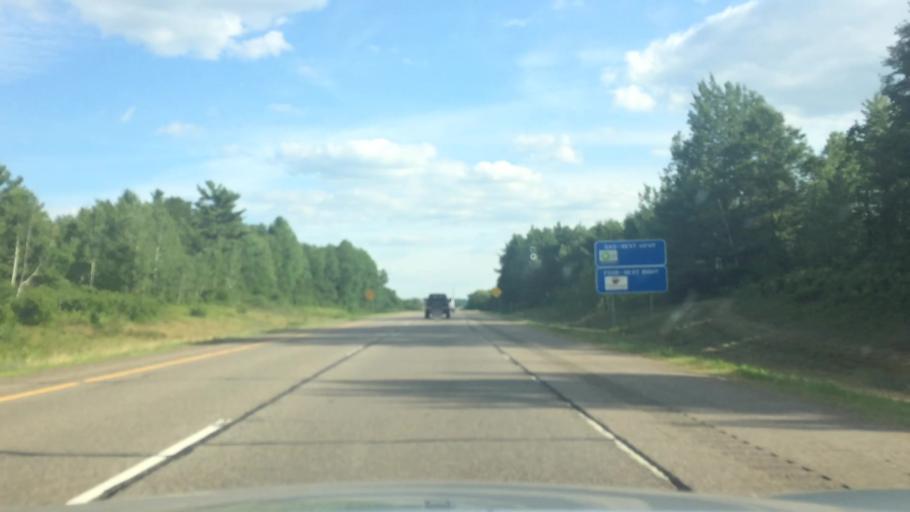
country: US
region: Wisconsin
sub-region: Lincoln County
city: Merrill
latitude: 45.1429
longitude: -89.6416
